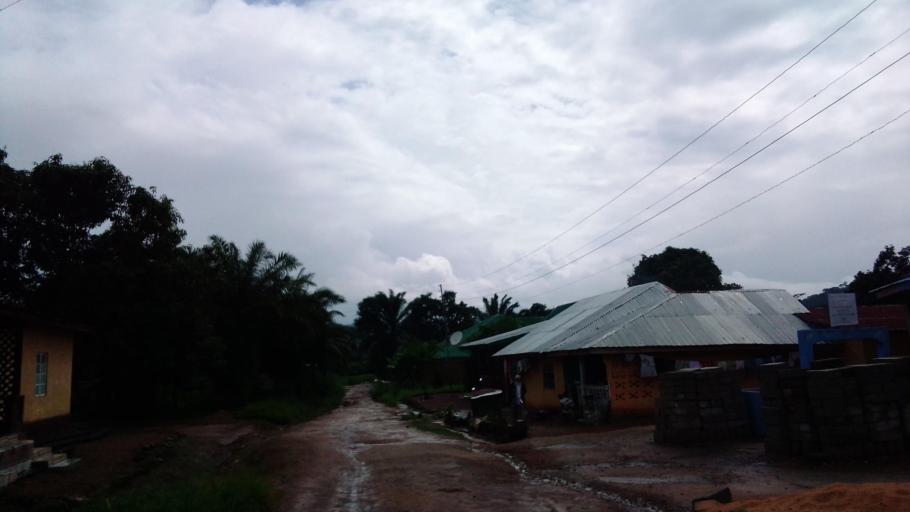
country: SL
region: Eastern Province
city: Kenema
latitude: 7.8539
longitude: -11.1977
